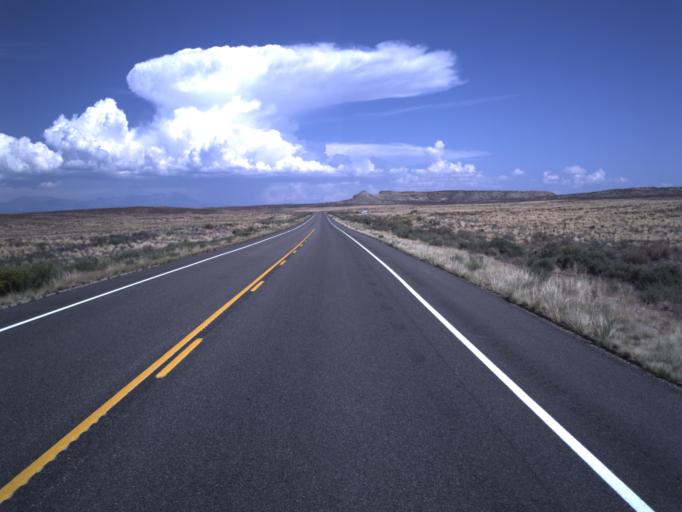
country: US
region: Utah
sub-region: San Juan County
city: Blanding
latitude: 37.3193
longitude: -109.5239
